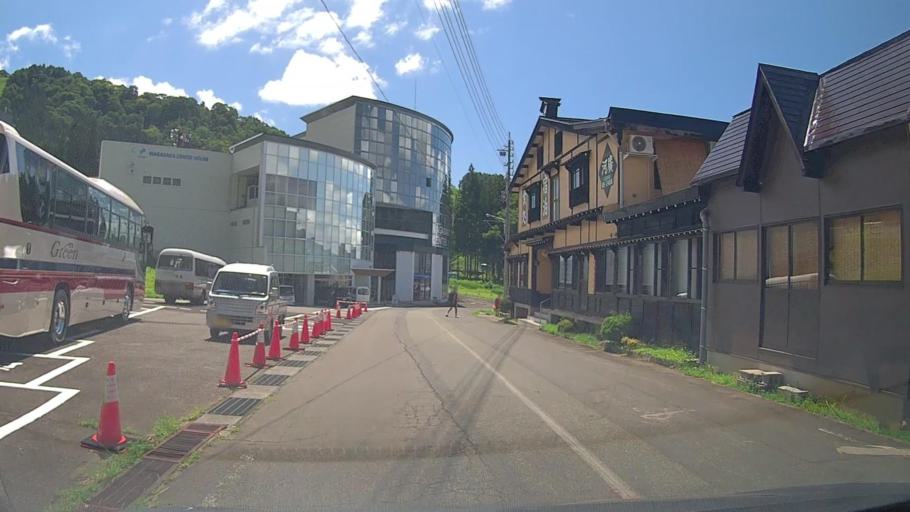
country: JP
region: Nagano
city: Iiyama
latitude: 36.9207
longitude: 138.4521
